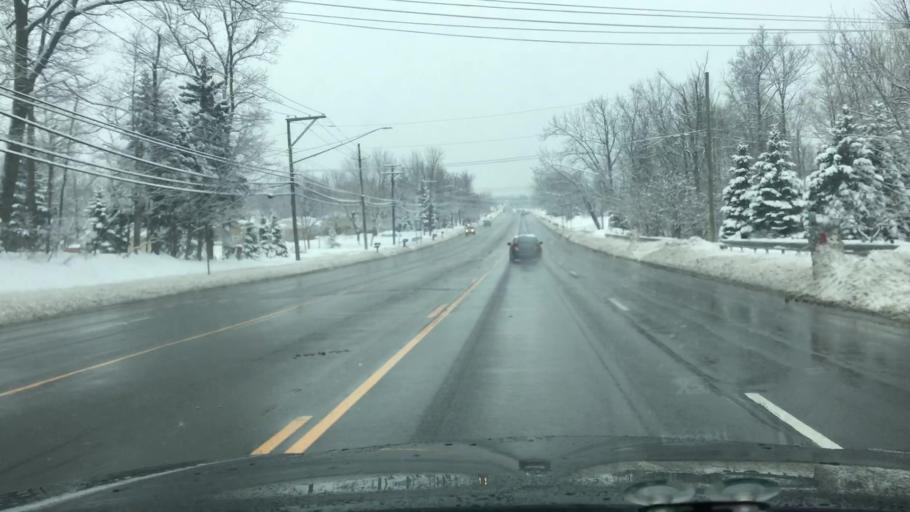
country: US
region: New York
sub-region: Erie County
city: Orchard Park
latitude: 42.8076
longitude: -78.7519
